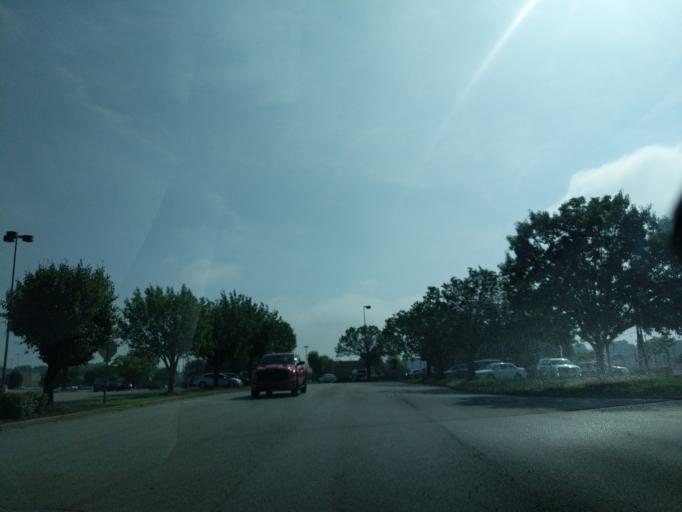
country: US
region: Tennessee
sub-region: Davidson County
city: Goodlettsville
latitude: 36.3013
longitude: -86.6954
